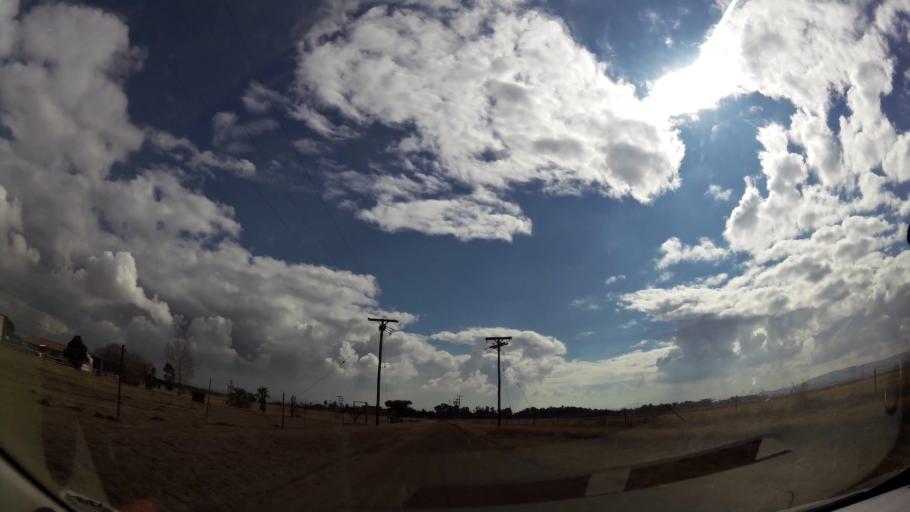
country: ZA
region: Gauteng
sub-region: Sedibeng District Municipality
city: Meyerton
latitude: -26.5994
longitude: 28.0929
